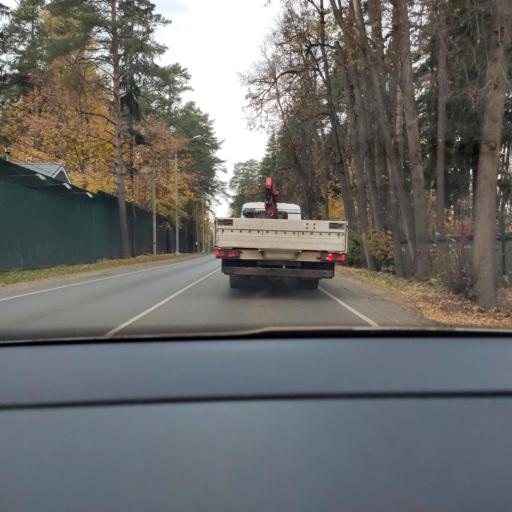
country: RU
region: Moskovskaya
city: Cherkizovo
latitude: 55.9704
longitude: 37.7761
